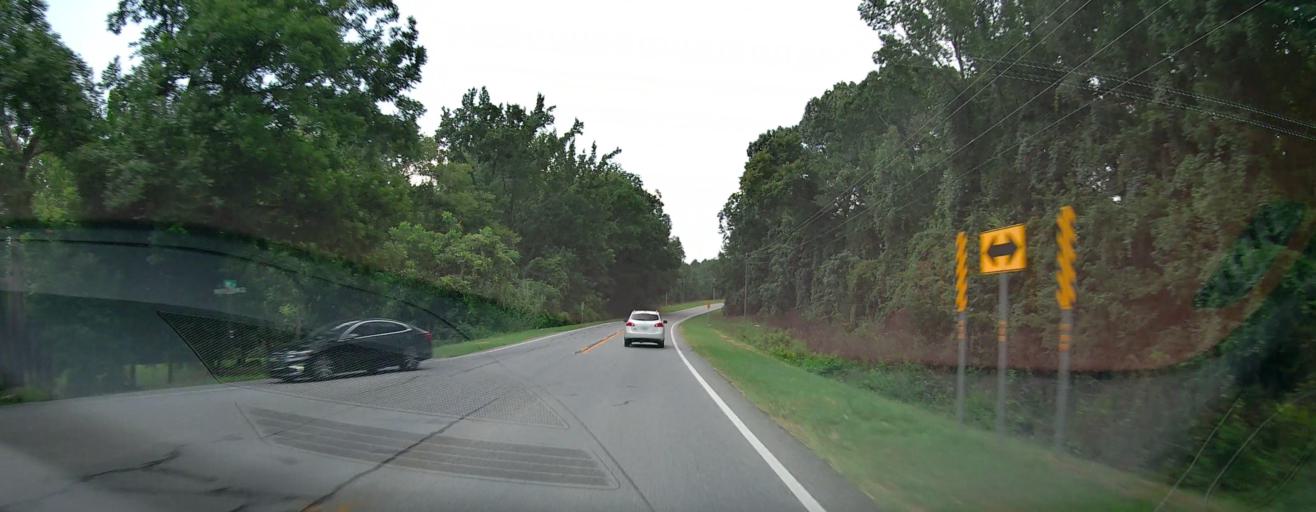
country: US
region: Georgia
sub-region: Laurens County
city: East Dublin
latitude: 32.5753
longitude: -82.8386
